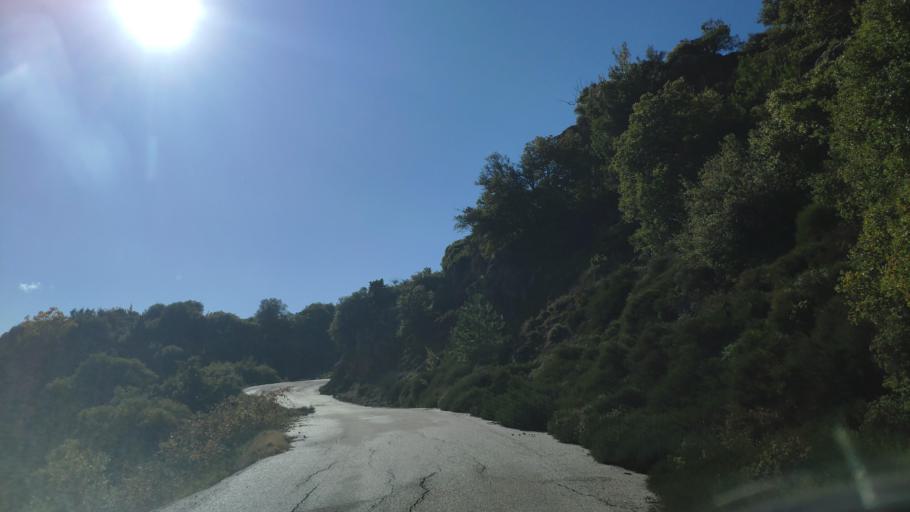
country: GR
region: West Greece
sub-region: Nomos Achaias
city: Aiyira
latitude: 38.0577
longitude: 22.4560
